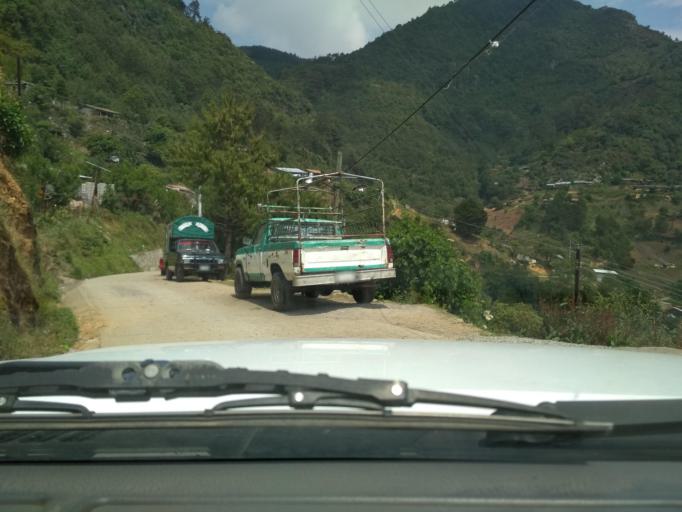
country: MX
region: Veracruz
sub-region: Camerino Z. Mendoza
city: Necoxtla
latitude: 18.7750
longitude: -97.1545
